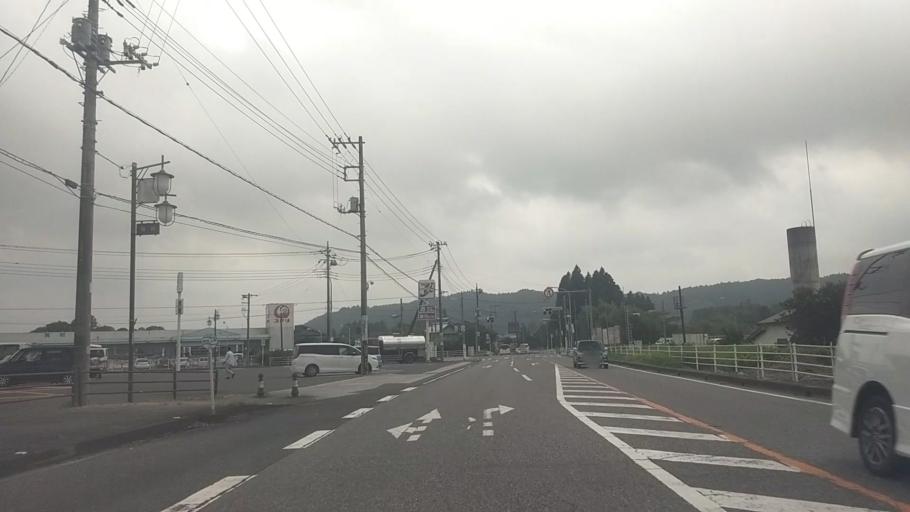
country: JP
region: Chiba
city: Ohara
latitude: 35.2821
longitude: 140.3051
